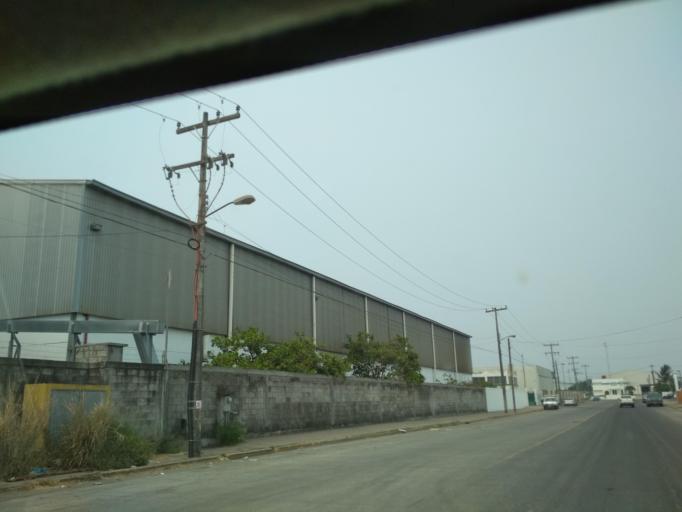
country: MX
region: Veracruz
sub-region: Veracruz
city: Las Amapolas
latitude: 19.1597
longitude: -96.2280
